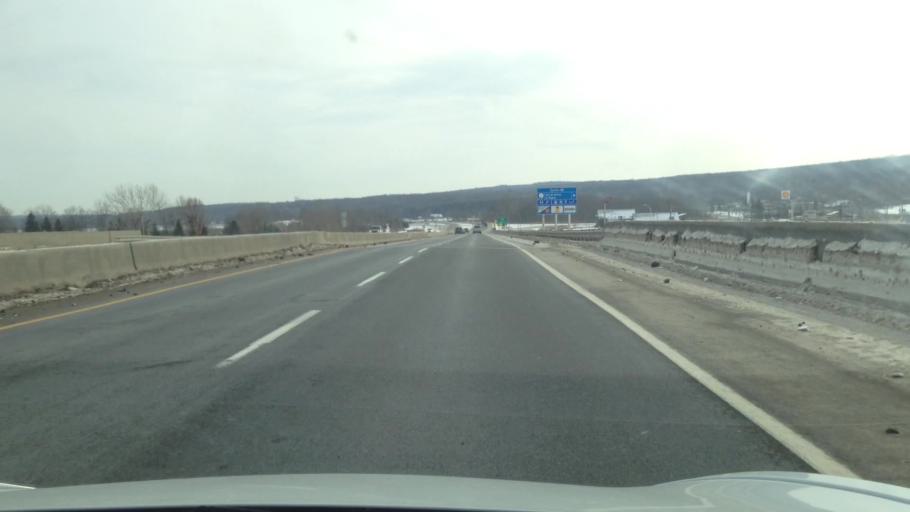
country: CA
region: Quebec
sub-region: Monteregie
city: Rigaud
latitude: 45.4817
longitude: -74.2876
